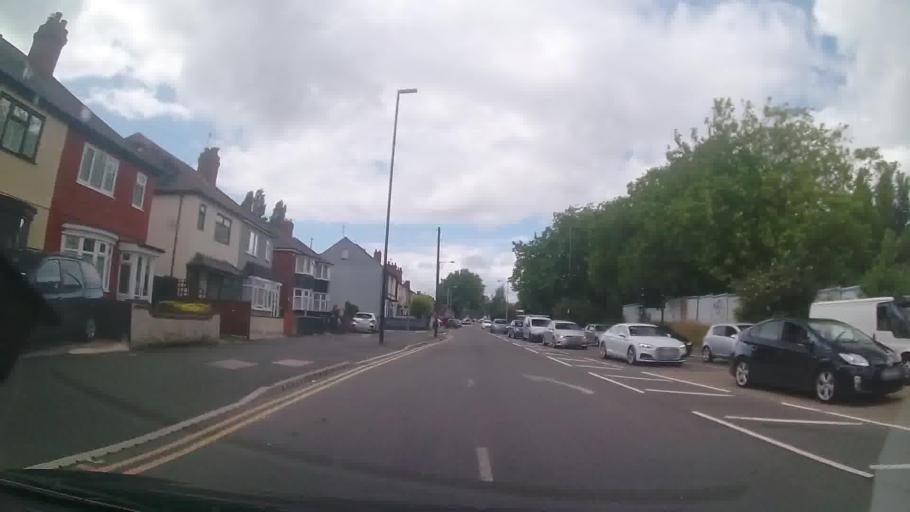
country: GB
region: England
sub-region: Walsall
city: Walsall
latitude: 52.5739
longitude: -2.0010
